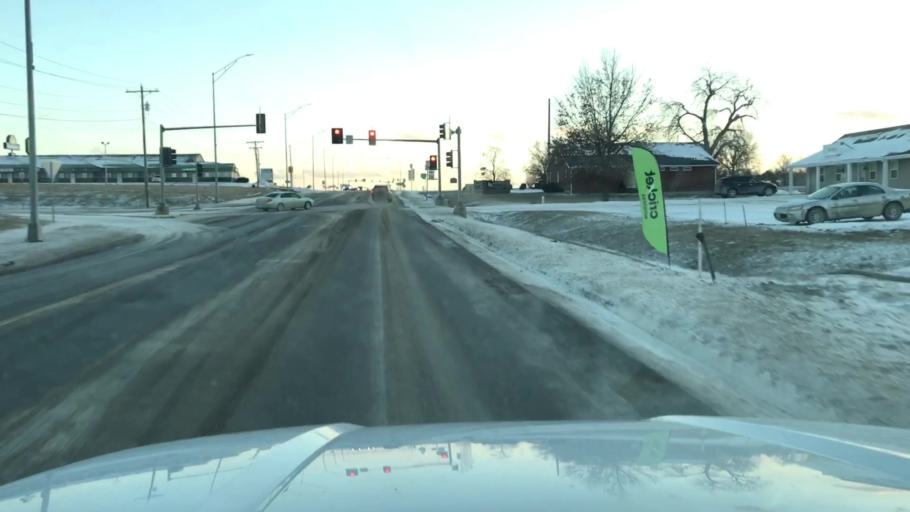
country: US
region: Missouri
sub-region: Clinton County
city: Cameron
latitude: 39.7586
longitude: -94.2344
